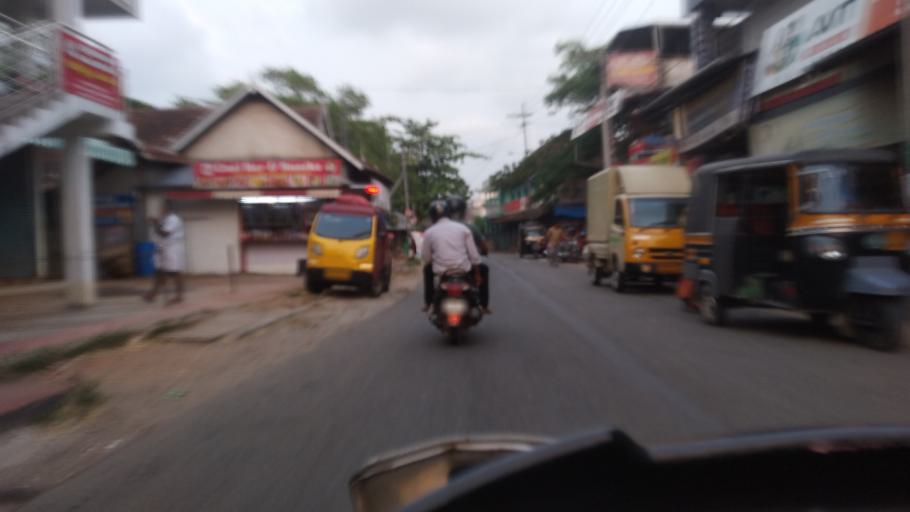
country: IN
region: Kerala
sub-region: Thrissur District
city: Kodungallur
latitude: 10.1511
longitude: 76.2200
